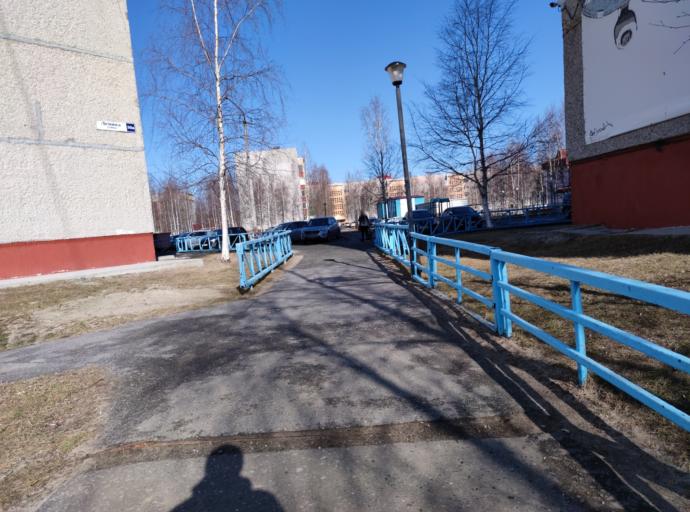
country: RU
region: Khanty-Mansiyskiy Avtonomnyy Okrug
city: Langepas
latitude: 61.2499
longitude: 75.1781
